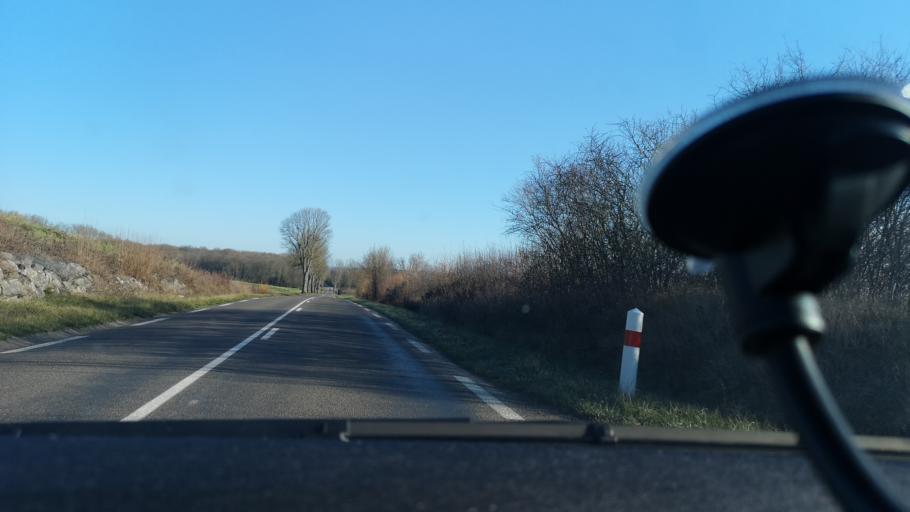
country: FR
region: Franche-Comte
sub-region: Departement du Jura
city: Bletterans
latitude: 46.7443
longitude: 5.4128
